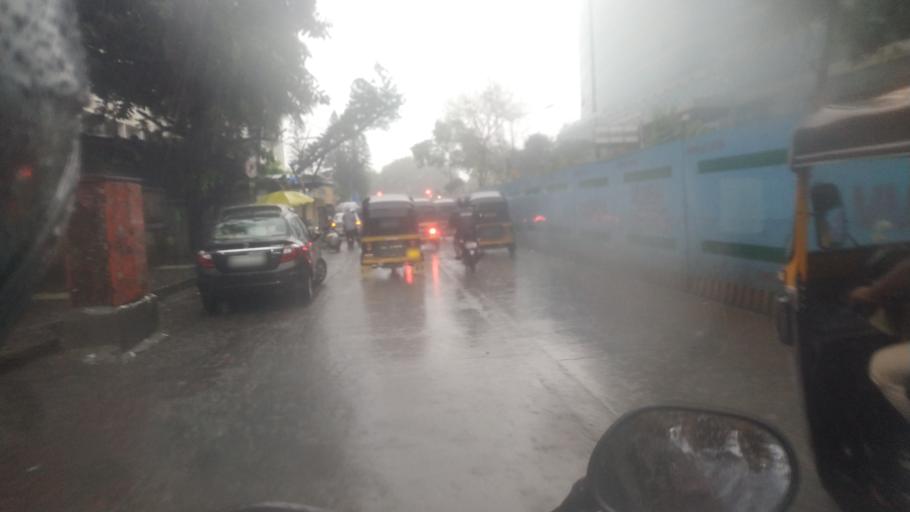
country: IN
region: Maharashtra
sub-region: Mumbai Suburban
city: Mumbai
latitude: 19.1040
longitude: 72.8370
